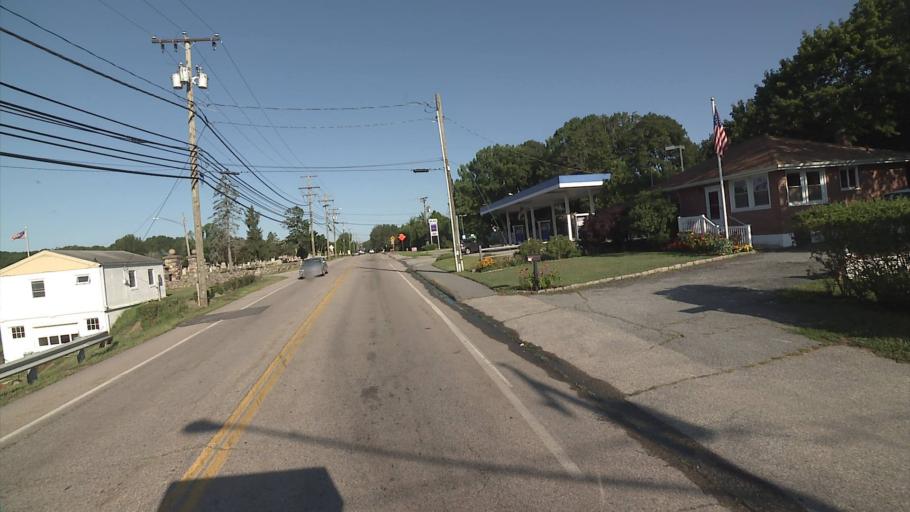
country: US
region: Connecticut
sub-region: New London County
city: Central Waterford
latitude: 41.3464
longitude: -72.1398
